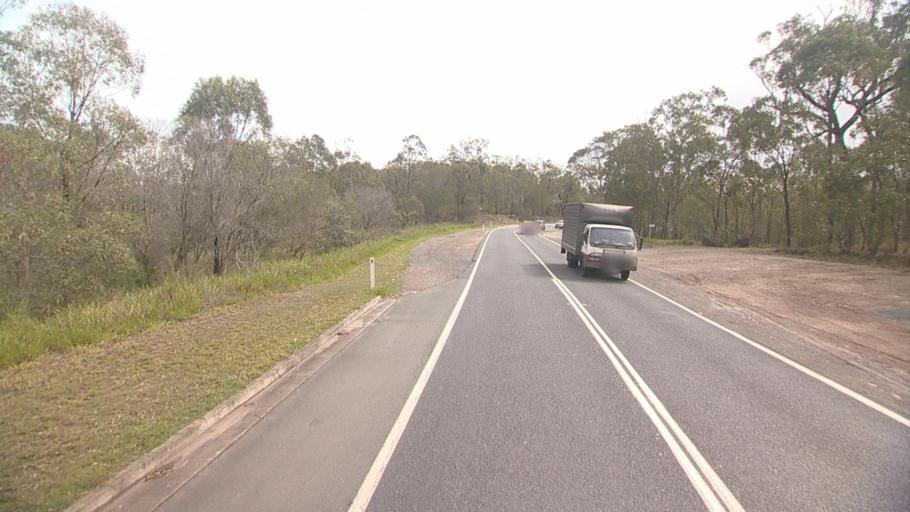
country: AU
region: Queensland
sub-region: Logan
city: Windaroo
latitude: -27.7292
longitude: 153.1859
